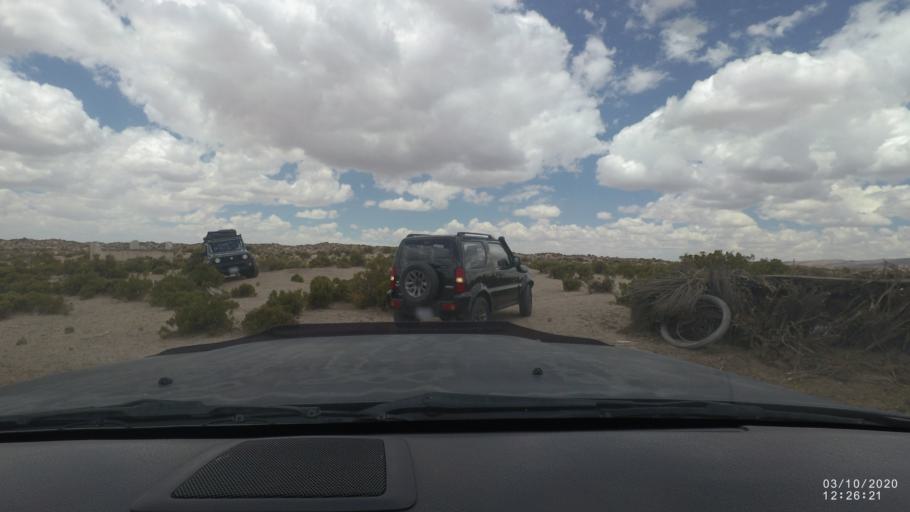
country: BO
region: Oruro
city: Poopo
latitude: -18.6934
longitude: -67.5535
